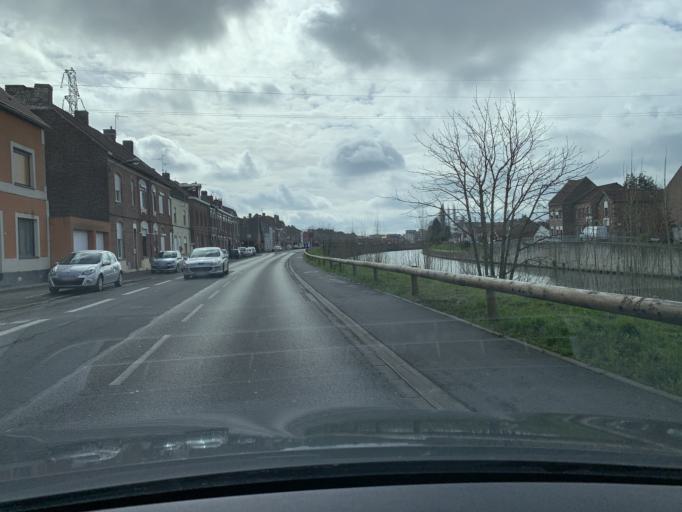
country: FR
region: Nord-Pas-de-Calais
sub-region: Departement du Nord
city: Douai
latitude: 50.3854
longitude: 3.0820
